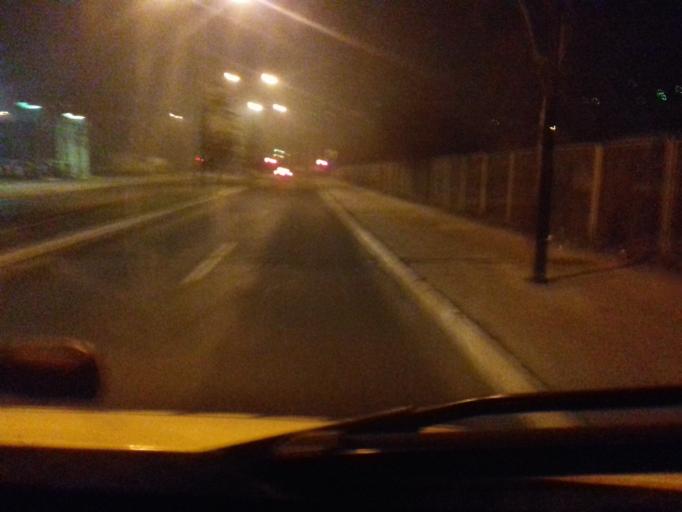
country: BA
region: Federation of Bosnia and Herzegovina
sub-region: Kanton Sarajevo
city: Sarajevo
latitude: 43.8470
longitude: 18.3472
